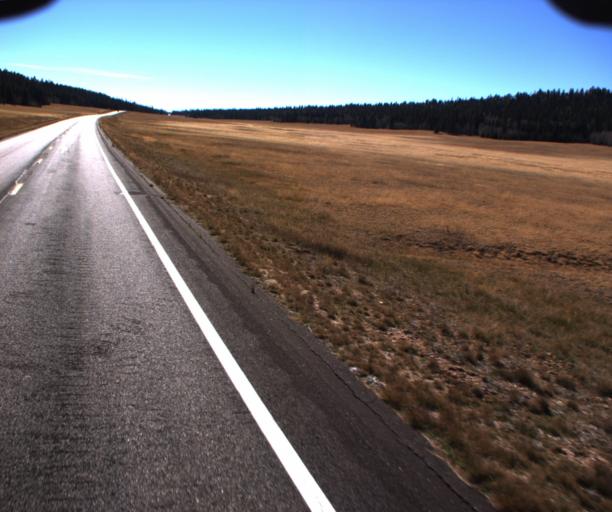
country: US
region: Arizona
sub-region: Coconino County
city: Grand Canyon
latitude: 36.3647
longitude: -112.1203
